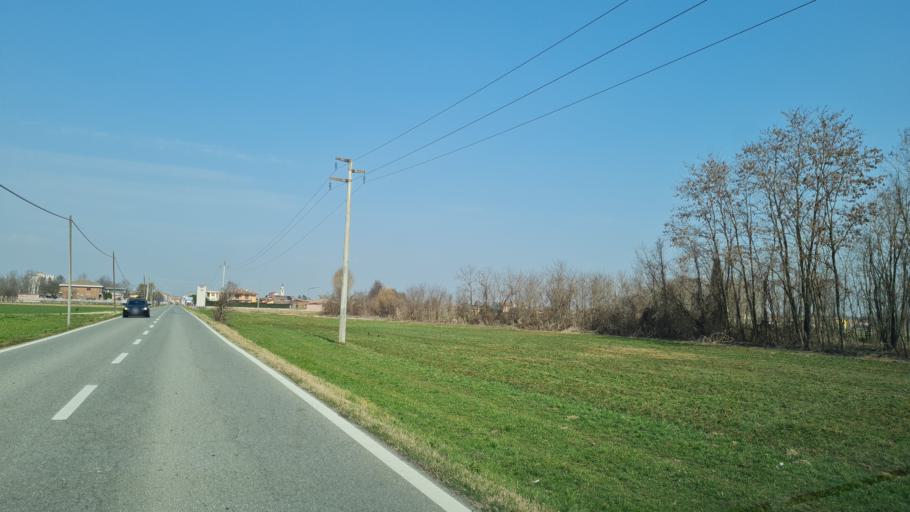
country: IT
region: Piedmont
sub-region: Provincia di Novara
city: Carpignano Sesia
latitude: 45.5243
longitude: 8.4180
